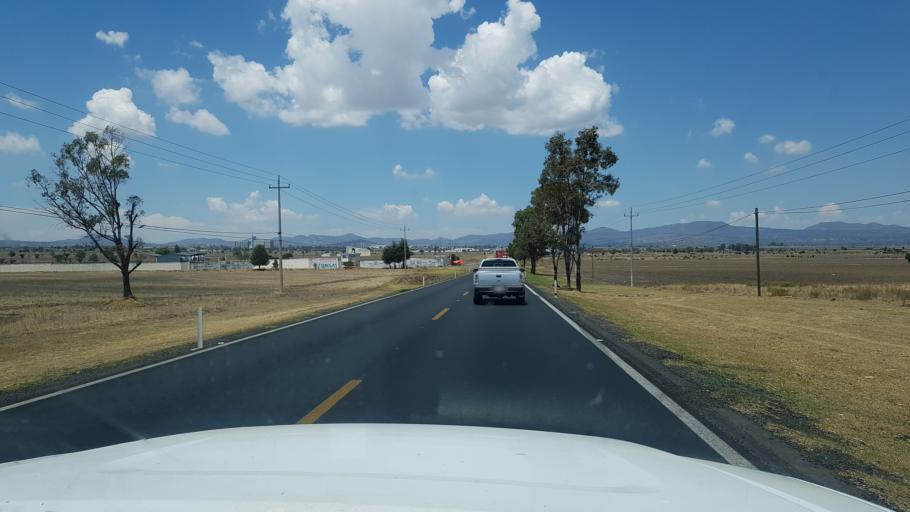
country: MX
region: Hidalgo
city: Calpulalpan
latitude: 19.5766
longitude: -98.5176
